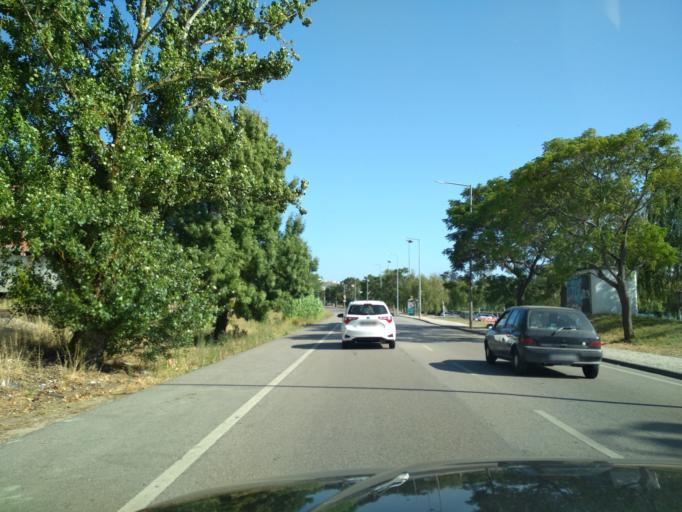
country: PT
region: Coimbra
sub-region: Coimbra
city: Coimbra
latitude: 40.2025
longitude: -8.4246
